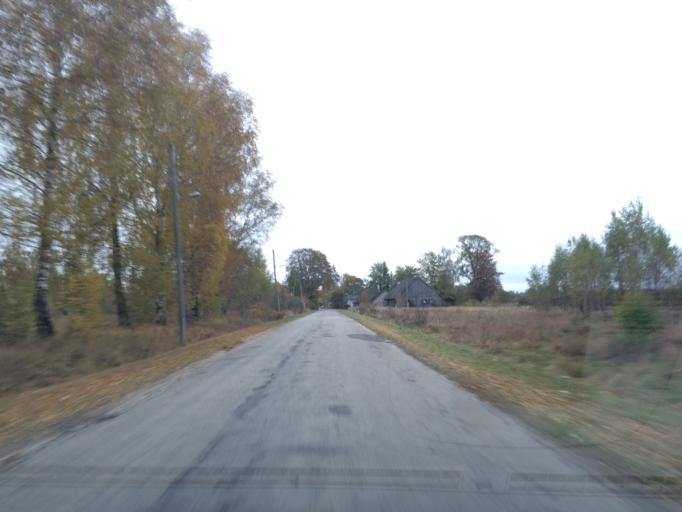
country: LV
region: Plavinu
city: Plavinas
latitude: 56.6150
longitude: 25.7673
